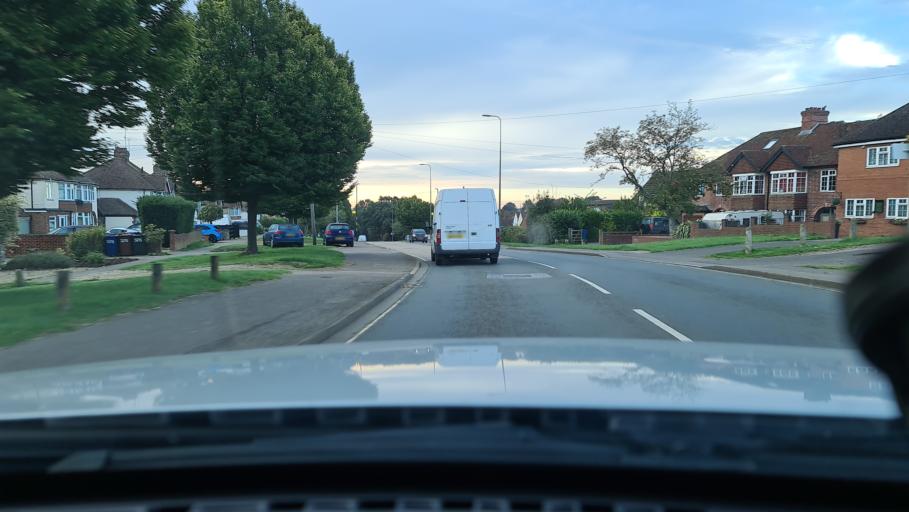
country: GB
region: England
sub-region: Oxfordshire
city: Banbury
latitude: 52.0683
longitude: -1.3601
